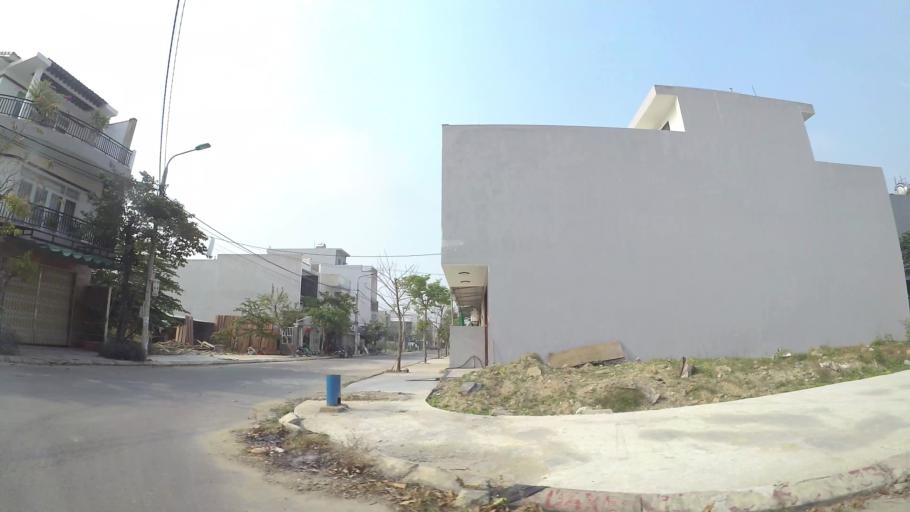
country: VN
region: Da Nang
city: Cam Le
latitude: 16.0087
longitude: 108.2262
